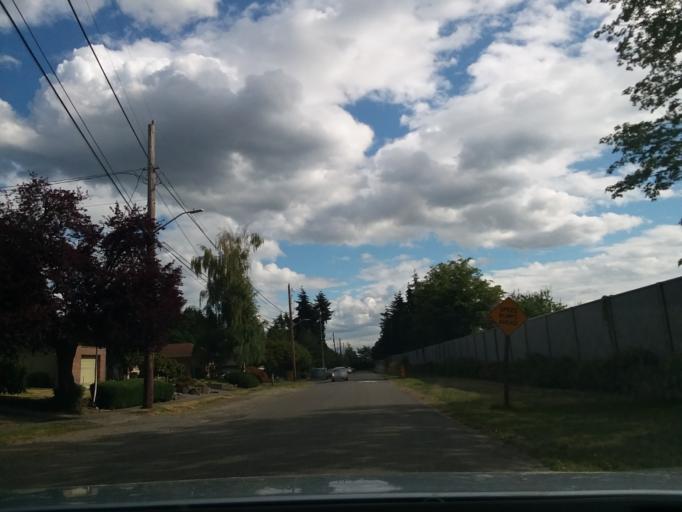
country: US
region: Washington
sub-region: King County
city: Shoreline
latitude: 47.6929
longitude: -122.3284
